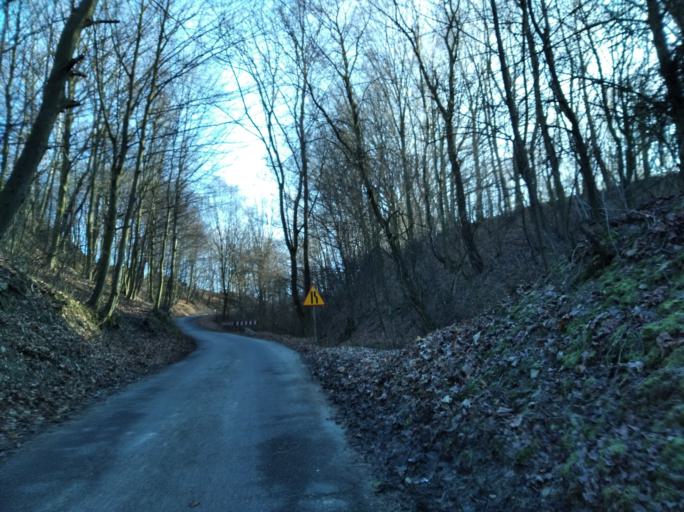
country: PL
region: Subcarpathian Voivodeship
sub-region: Powiat strzyzowski
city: Wysoka Strzyzowska
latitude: 49.8570
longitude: 21.7415
